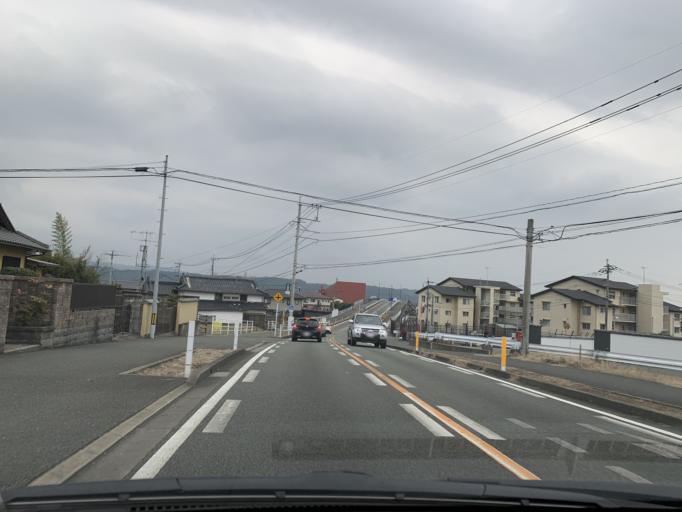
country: JP
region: Kumamoto
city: Ozu
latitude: 32.8791
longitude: 130.8768
